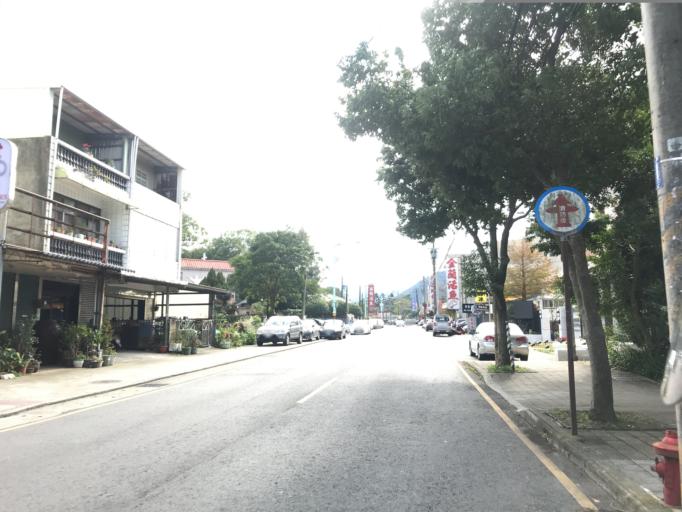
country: TW
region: Taiwan
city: Daxi
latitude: 24.8401
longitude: 121.2405
